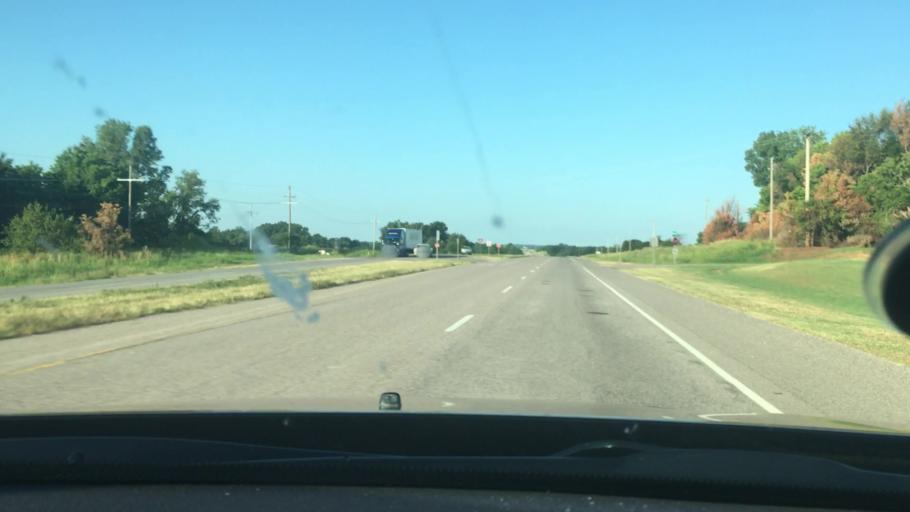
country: US
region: Oklahoma
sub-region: Pontotoc County
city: Ada
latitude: 34.6763
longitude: -96.7743
